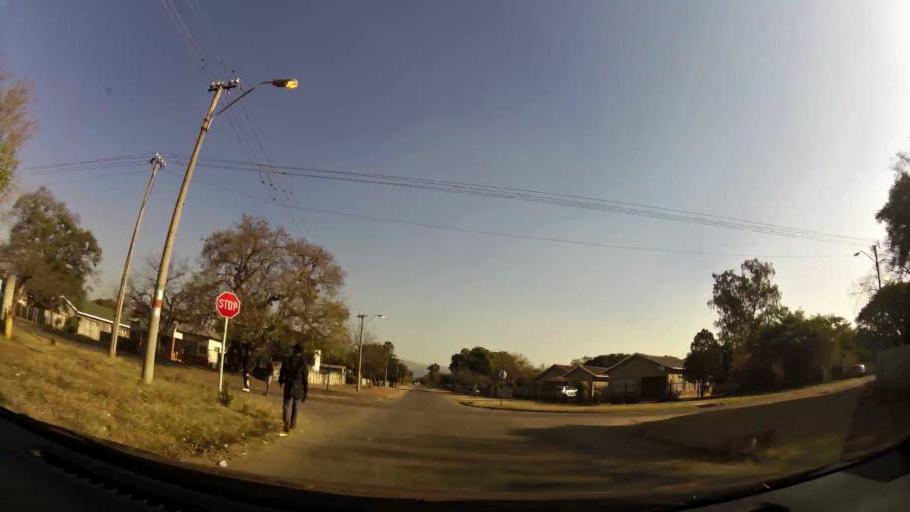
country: ZA
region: North-West
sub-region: Bojanala Platinum District Municipality
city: Rustenburg
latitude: -25.6478
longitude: 27.2303
